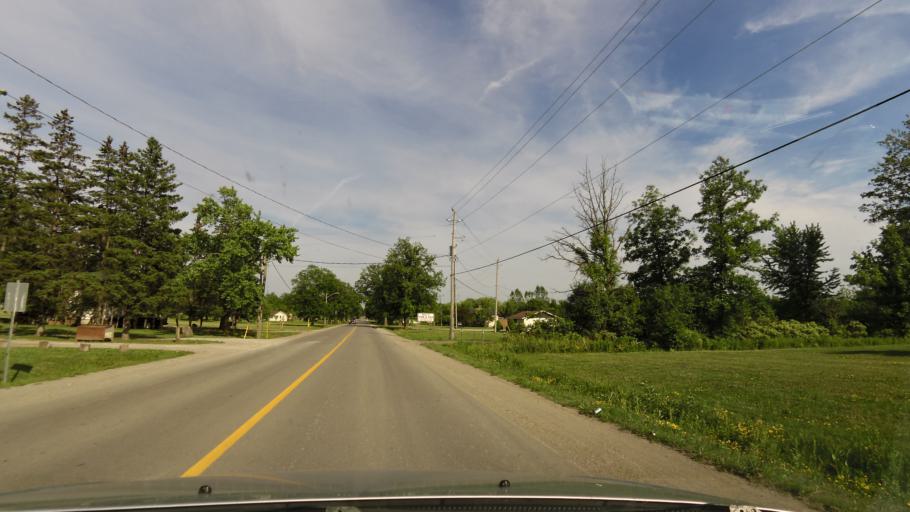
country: CA
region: Ontario
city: Brantford
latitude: 43.0672
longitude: -80.1138
